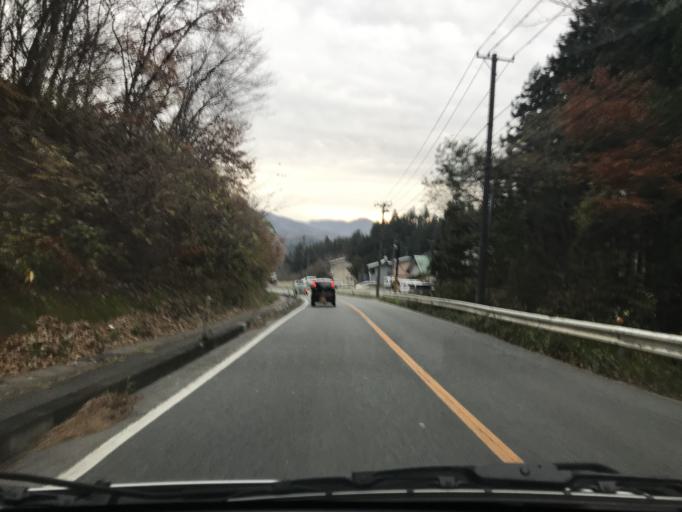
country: JP
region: Iwate
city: Ichinoseki
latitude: 39.0015
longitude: 141.3242
